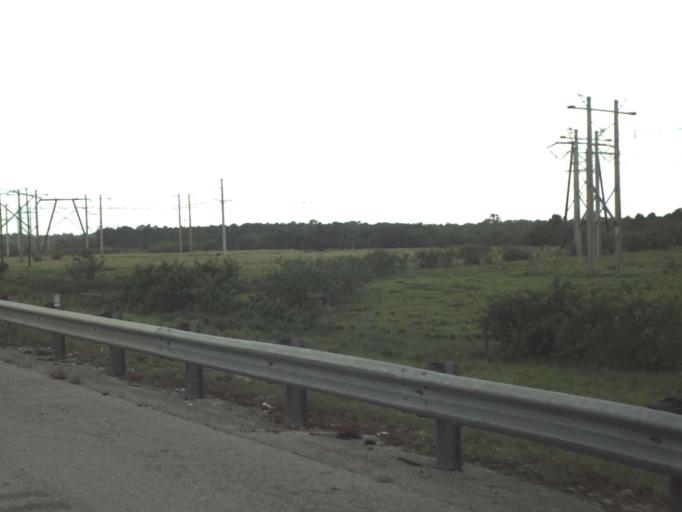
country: US
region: Florida
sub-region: Saint Lucie County
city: Fort Pierce South
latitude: 27.3589
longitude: -80.4143
